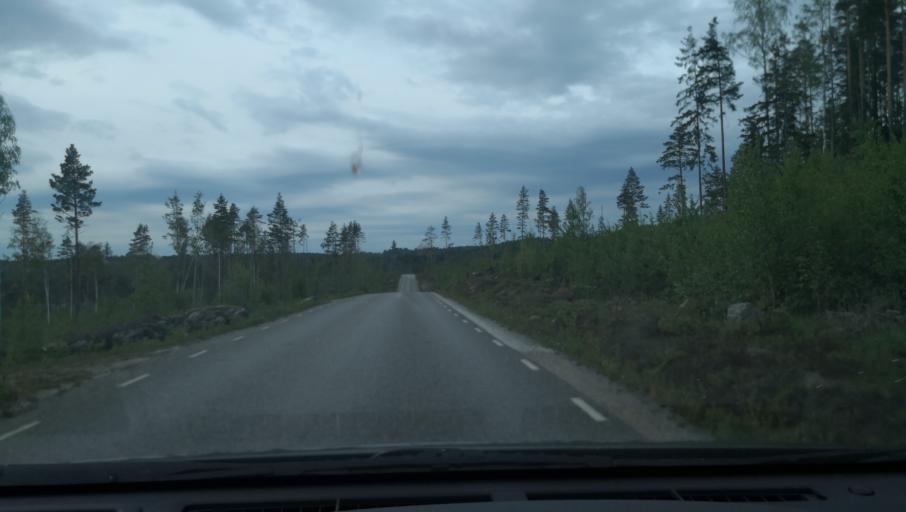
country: SE
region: Vaestmanland
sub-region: Skinnskattebergs Kommun
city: Skinnskatteberg
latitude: 59.8264
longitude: 15.5801
